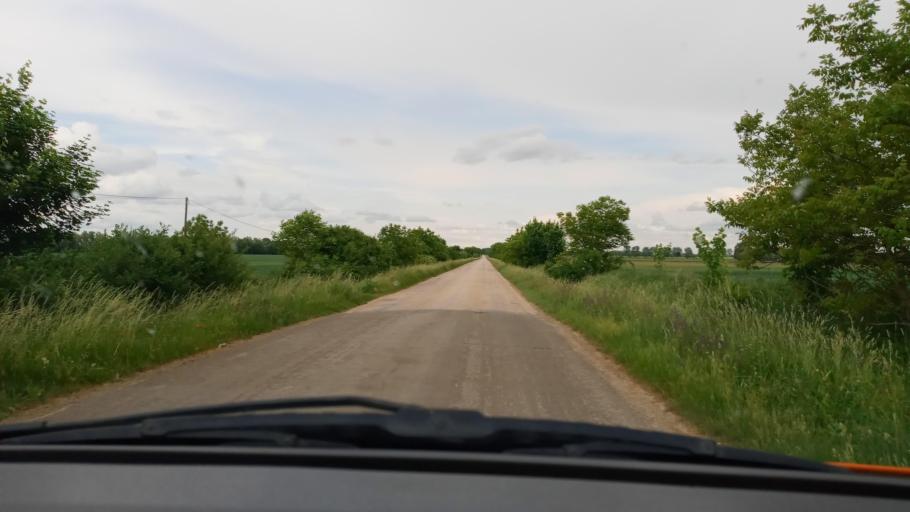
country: HU
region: Baranya
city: Harkany
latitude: 45.9123
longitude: 18.1432
